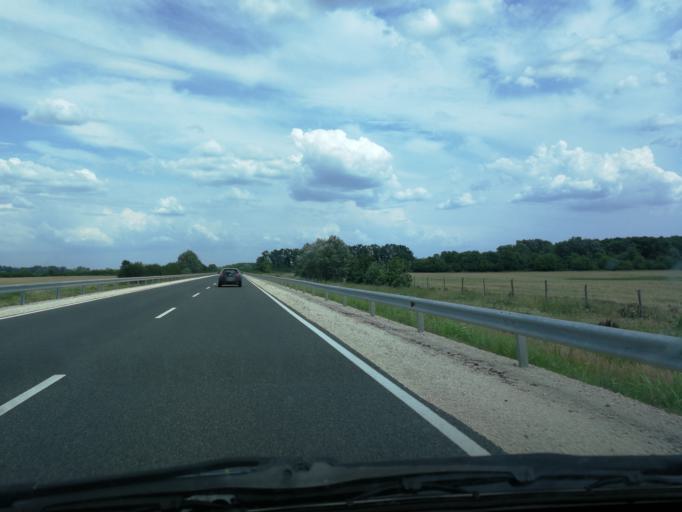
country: HU
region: Bacs-Kiskun
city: Dusnok
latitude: 46.3526
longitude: 18.9238
